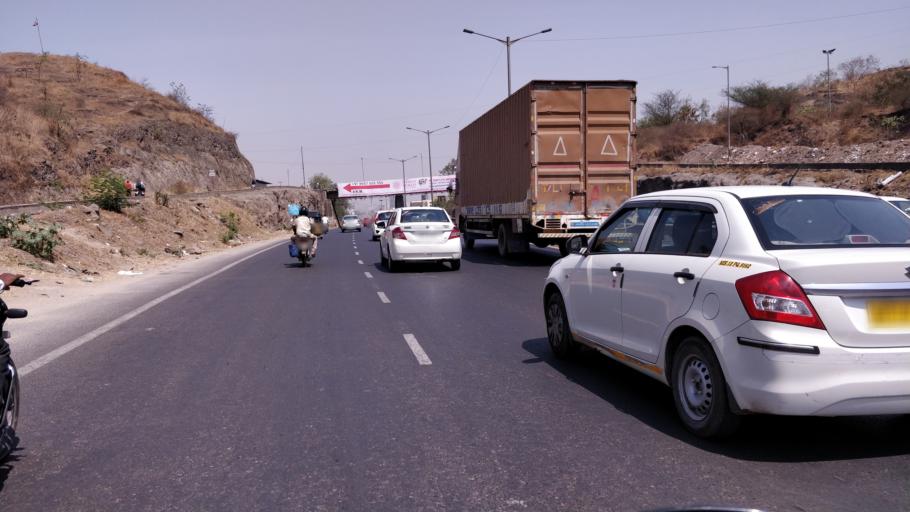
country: IN
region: Maharashtra
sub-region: Pune Division
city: Shivaji Nagar
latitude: 18.5454
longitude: 73.7742
